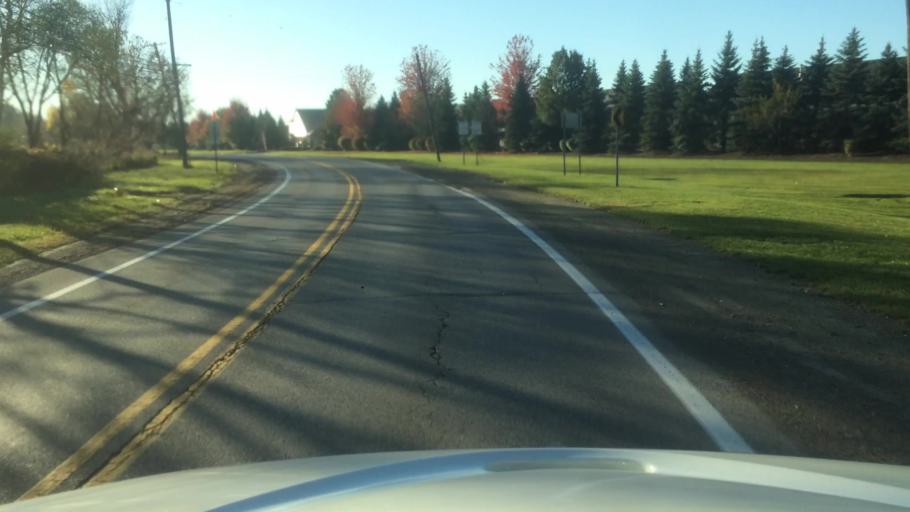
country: US
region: Michigan
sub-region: Macomb County
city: Shelby
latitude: 42.6851
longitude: -82.9516
